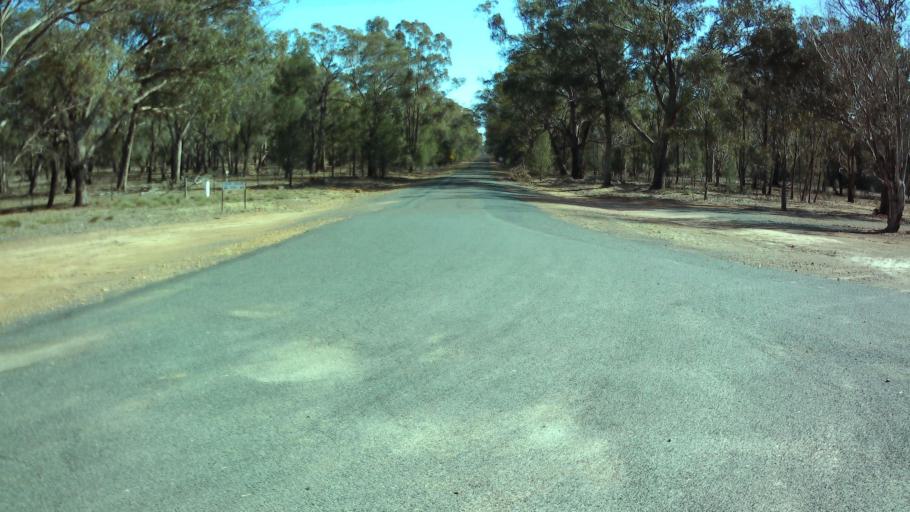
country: AU
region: New South Wales
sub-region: Weddin
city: Grenfell
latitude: -33.8153
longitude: 147.9533
